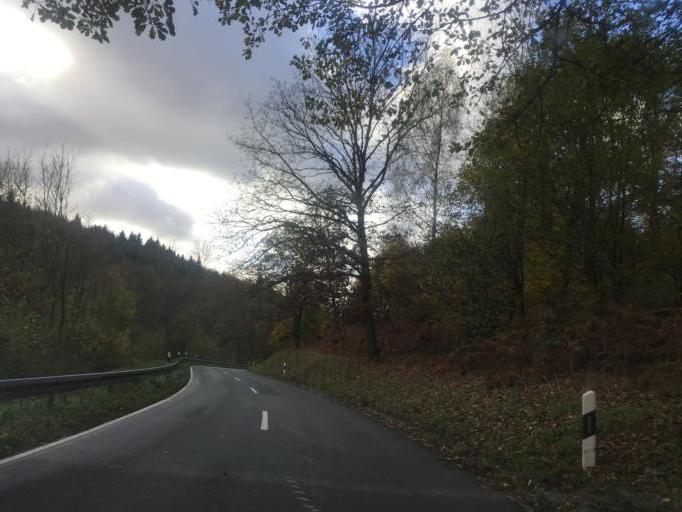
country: DE
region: Lower Saxony
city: Furstenberg
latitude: 51.7542
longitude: 9.4422
